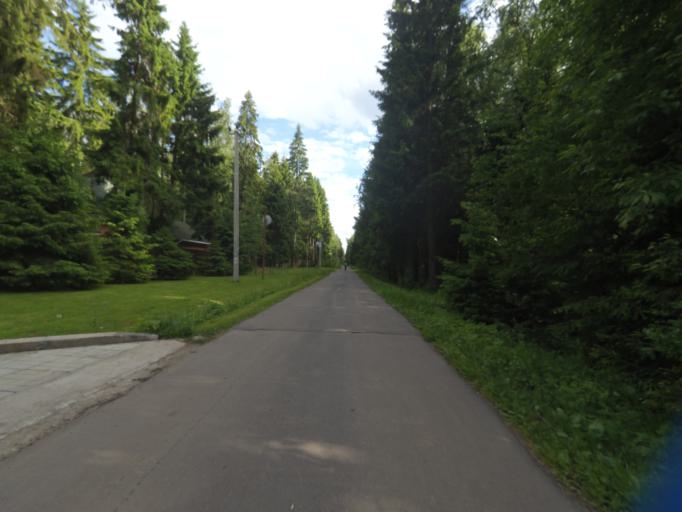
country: RU
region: Moskovskaya
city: Nekrasovskiy
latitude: 56.1149
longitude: 37.5172
